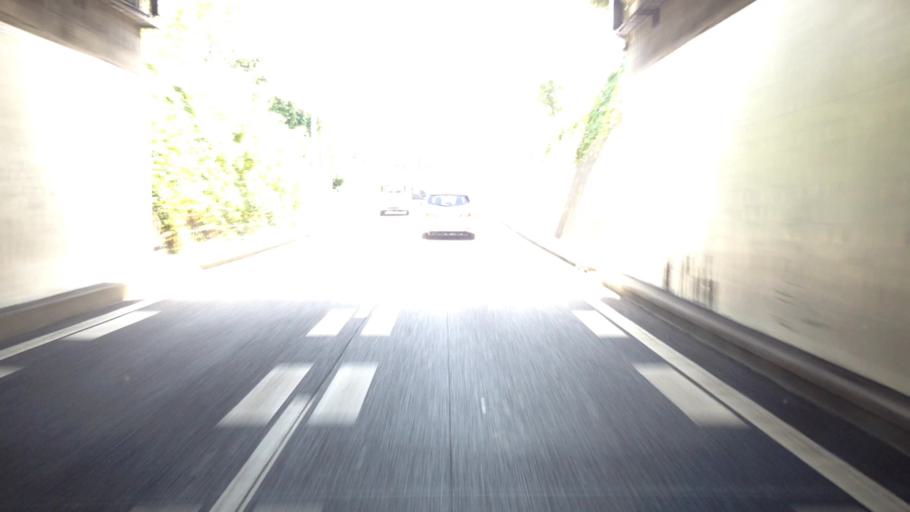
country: JP
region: Kanagawa
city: Yokohama
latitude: 35.4789
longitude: 139.5962
